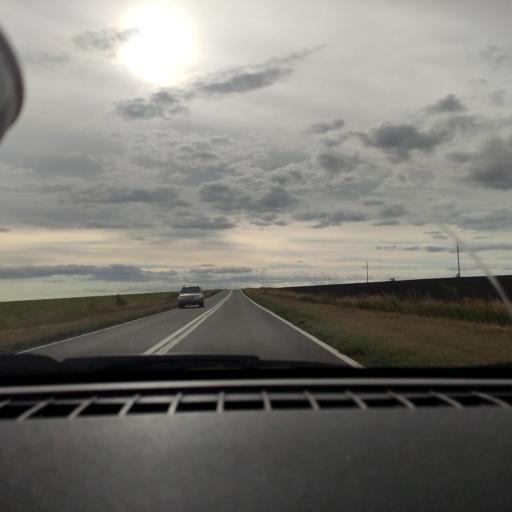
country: RU
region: Samara
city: Georgiyevka
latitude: 53.4169
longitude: 50.9025
